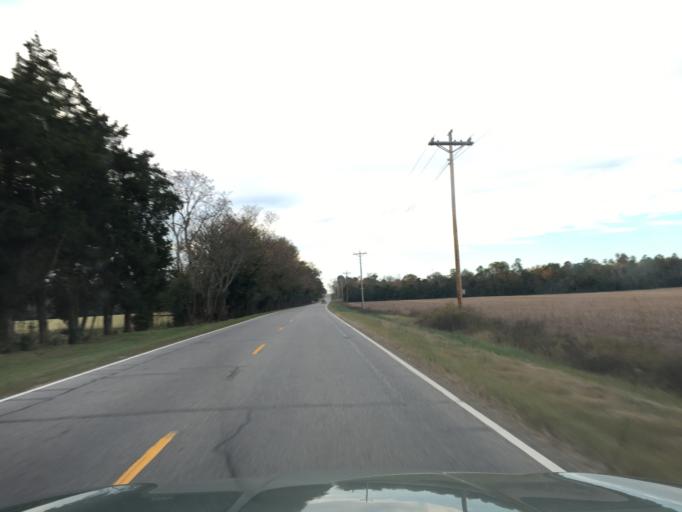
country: US
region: South Carolina
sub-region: Lexington County
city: Leesville
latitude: 33.7658
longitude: -81.3822
